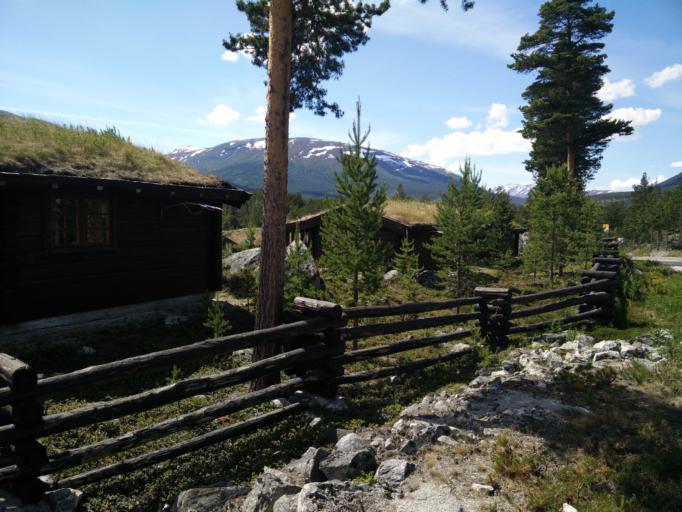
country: NO
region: Oppland
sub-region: Skjak
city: Bismo
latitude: 61.9171
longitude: 8.0934
